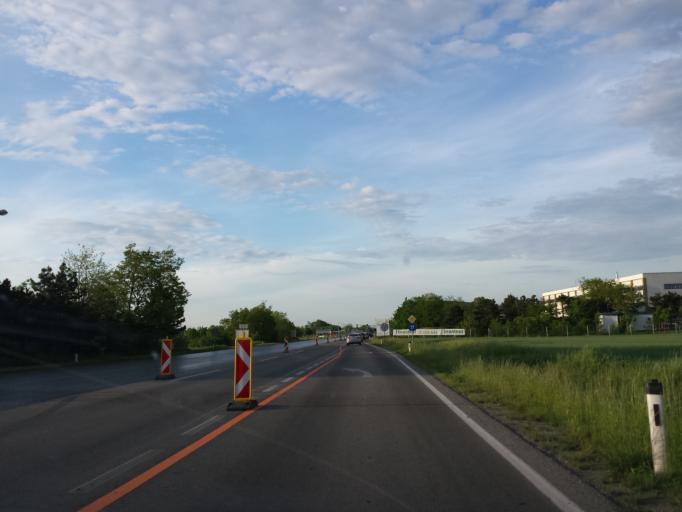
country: AT
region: Lower Austria
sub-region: Politischer Bezirk Baden
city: Traiskirchen
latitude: 47.9928
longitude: 16.2978
